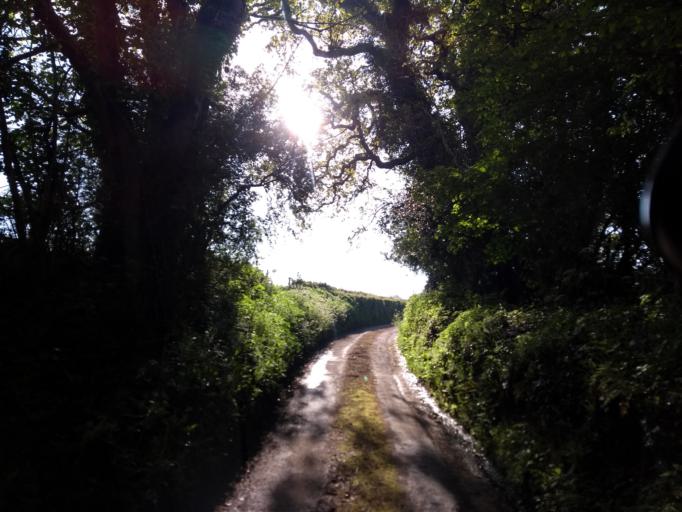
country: GB
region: England
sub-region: Dorset
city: Lyme Regis
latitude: 50.7989
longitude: -2.9110
